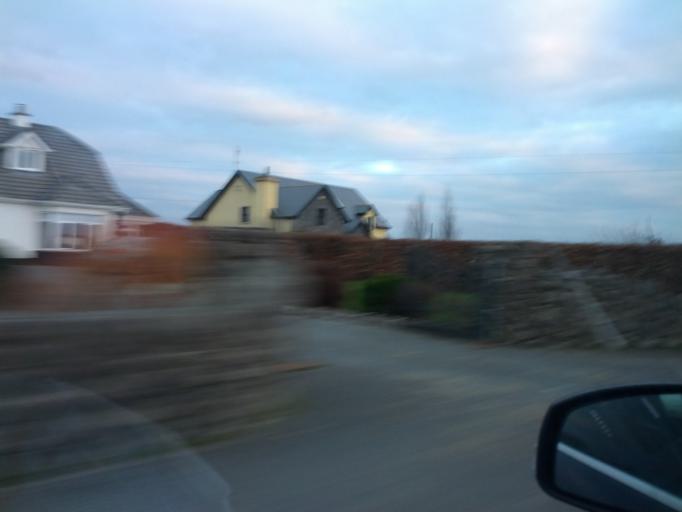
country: IE
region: Connaught
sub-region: County Galway
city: Athenry
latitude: 53.3278
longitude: -8.7660
